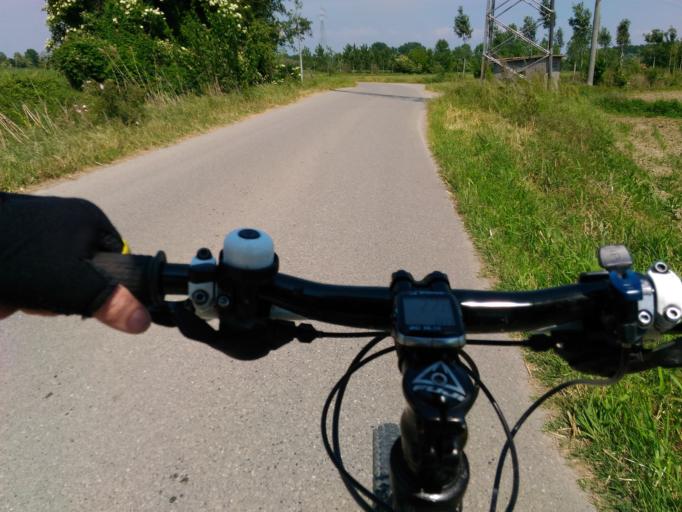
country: IT
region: Lombardy
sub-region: Provincia di Lodi
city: Montanaso Lombardo
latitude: 45.3455
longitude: 9.4715
